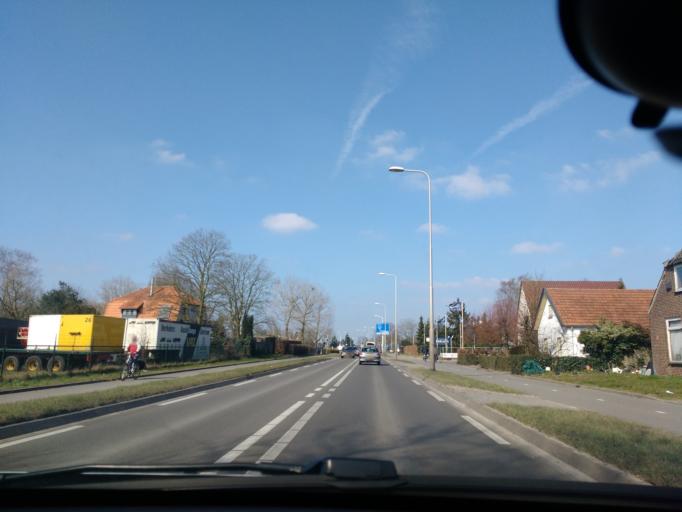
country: NL
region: North Brabant
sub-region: Gemeente Cuijk
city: Cuijk
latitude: 51.7688
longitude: 5.8649
